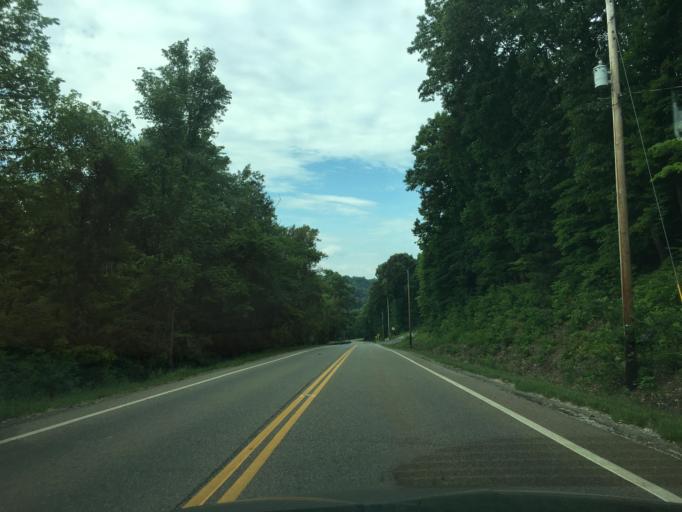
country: US
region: Ohio
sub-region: Tuscarawas County
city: New Philadelphia
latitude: 40.5241
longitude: -81.4259
